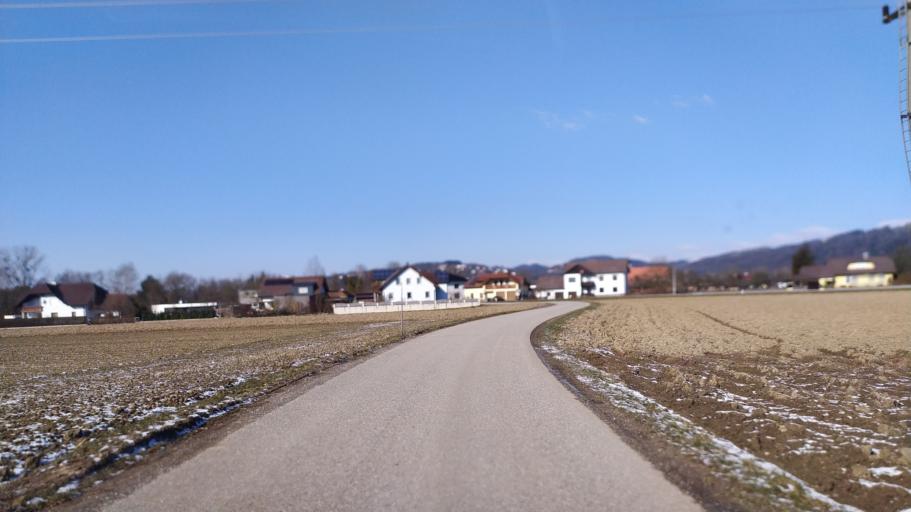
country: AT
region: Upper Austria
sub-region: Politischer Bezirk Urfahr-Umgebung
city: Feldkirchen an der Donau
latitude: 48.3454
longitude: 14.0750
